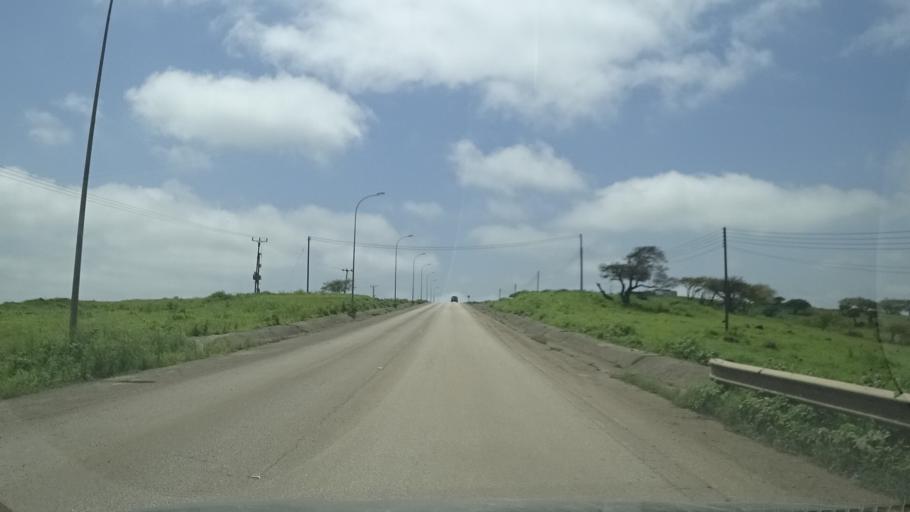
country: OM
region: Zufar
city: Salalah
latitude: 17.2205
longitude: 54.2573
